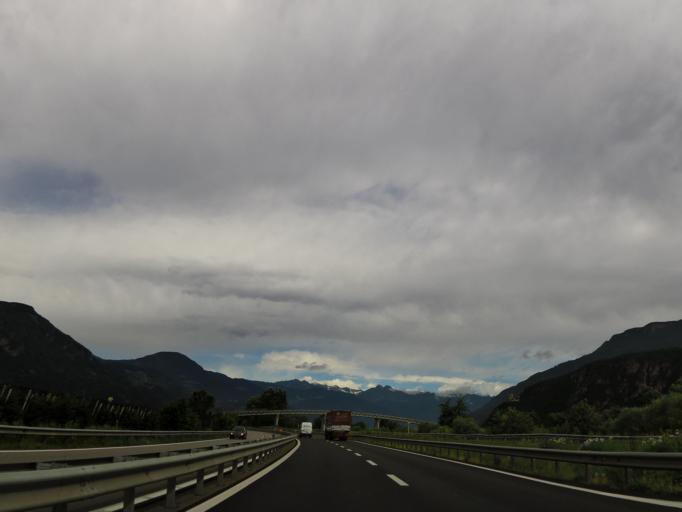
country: IT
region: Trentino-Alto Adige
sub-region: Bolzano
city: Terlano
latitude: 46.5095
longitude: 11.2626
